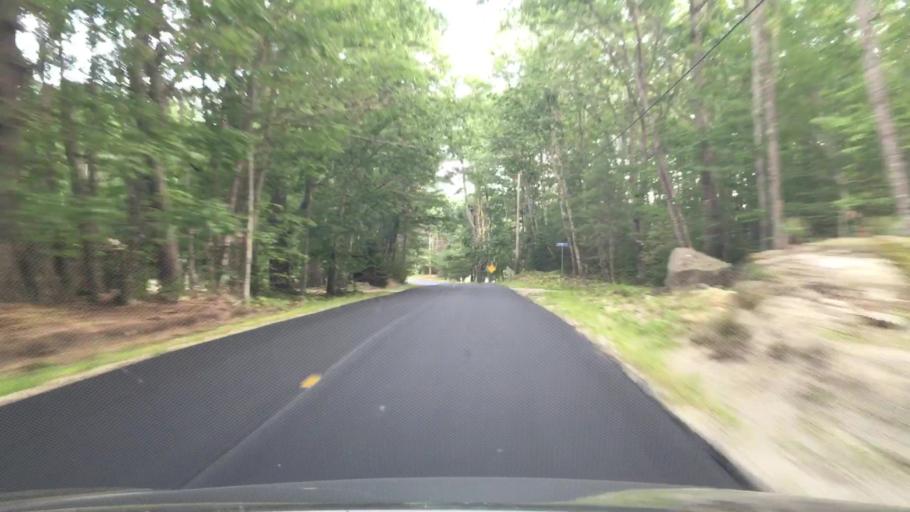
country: US
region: Maine
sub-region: Hancock County
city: Surry
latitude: 44.5200
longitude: -68.6079
